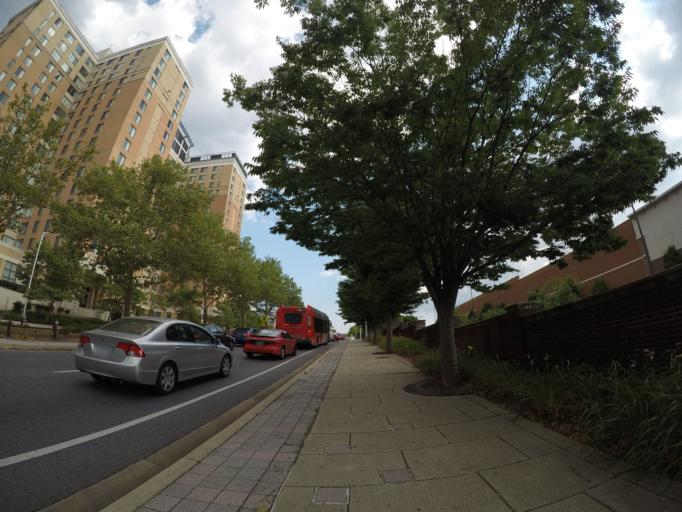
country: US
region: Maryland
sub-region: Prince George's County
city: University Park
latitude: 38.9693
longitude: -76.9541
